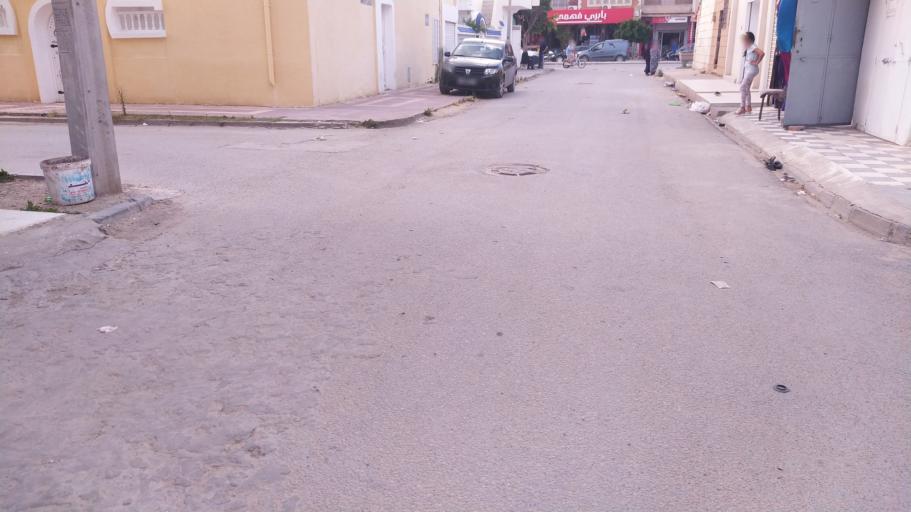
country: TN
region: Al Qayrawan
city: Kairouan
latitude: 35.6699
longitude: 10.0836
